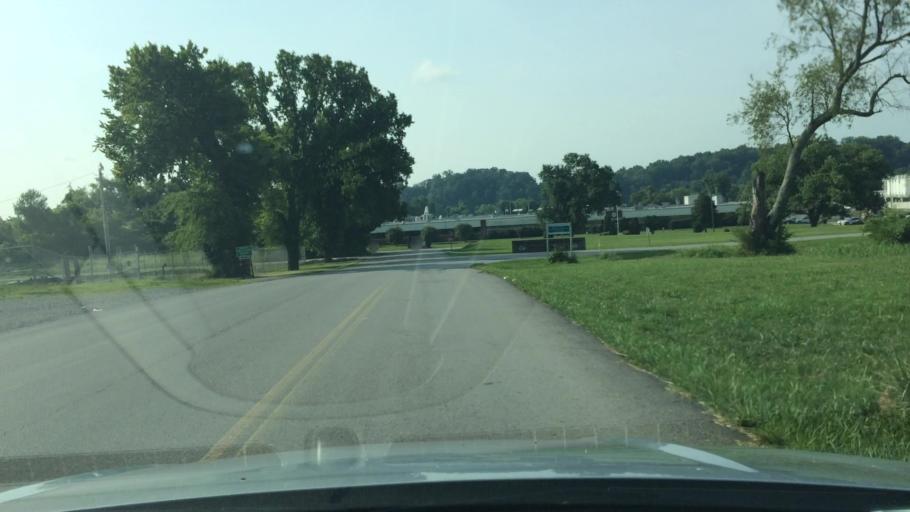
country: US
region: Tennessee
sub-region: Loudon County
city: Lenoir City
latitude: 35.7887
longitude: -84.2667
